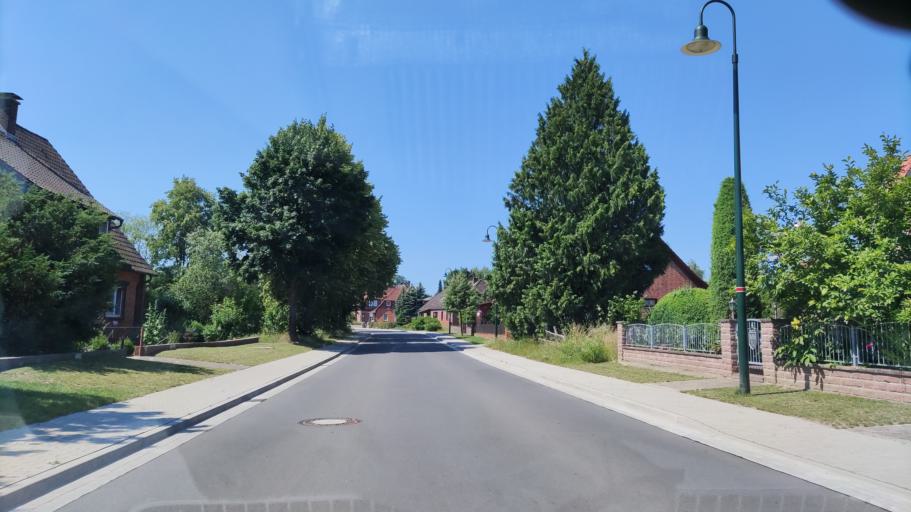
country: DE
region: Lower Saxony
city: Suderburg
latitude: 52.8787
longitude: 10.4102
